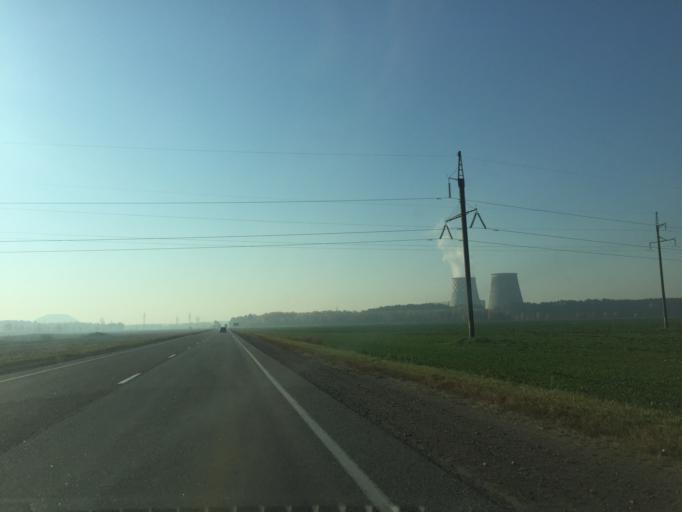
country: BY
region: Gomel
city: Kastsyukowka
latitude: 52.4611
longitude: 30.8246
